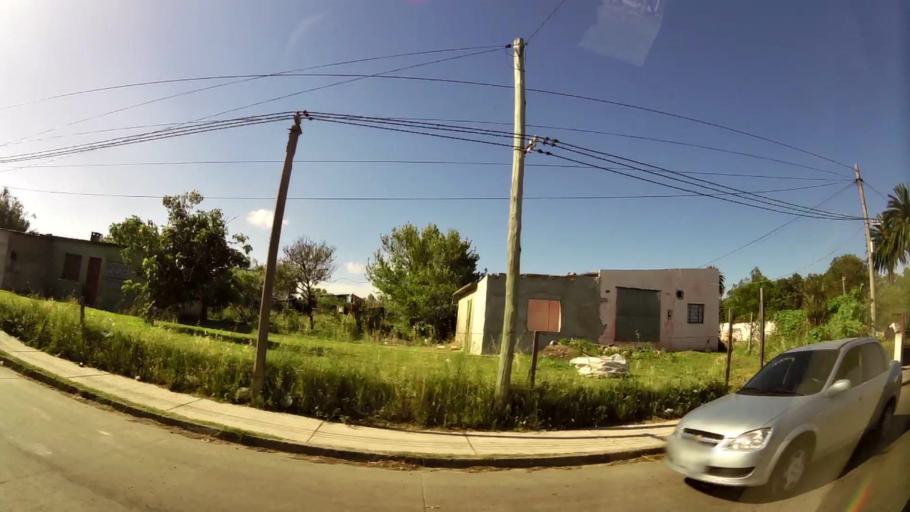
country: UY
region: Montevideo
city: Montevideo
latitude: -34.8354
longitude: -56.1669
